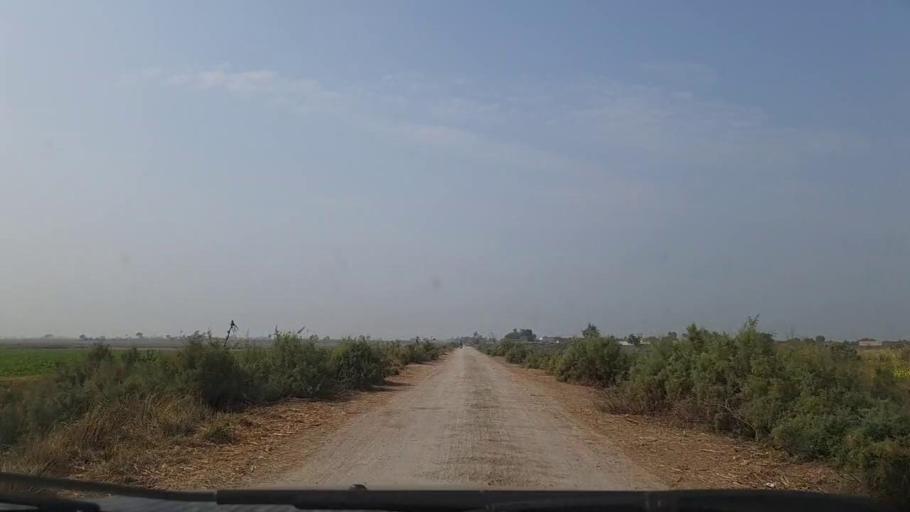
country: PK
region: Sindh
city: Sanghar
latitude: 26.0753
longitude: 68.9541
